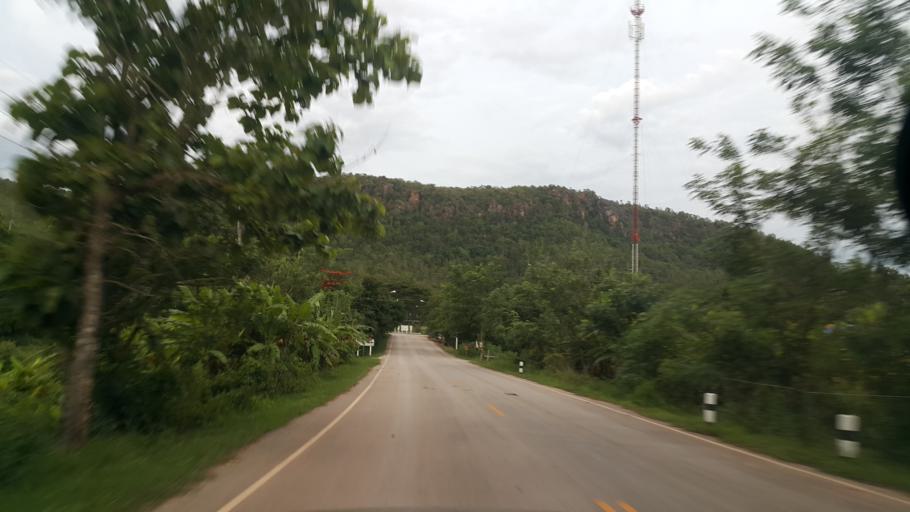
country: TH
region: Loei
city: Na Haeo
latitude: 17.4942
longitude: 101.1827
